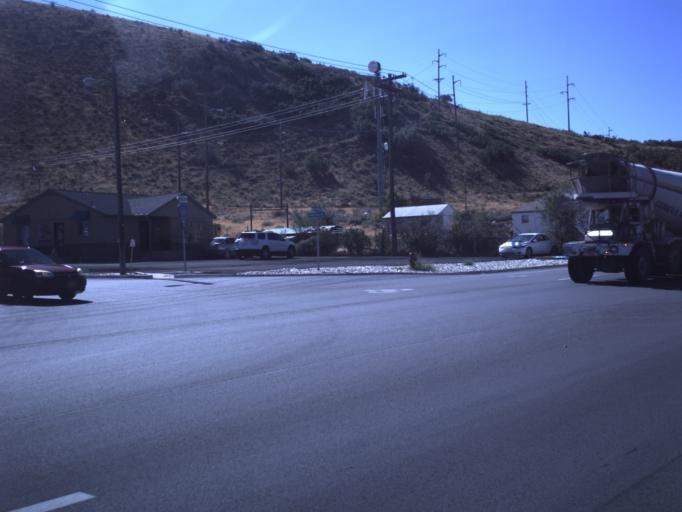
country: US
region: Utah
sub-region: Tooele County
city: Tooele
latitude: 40.5212
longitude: -112.2989
